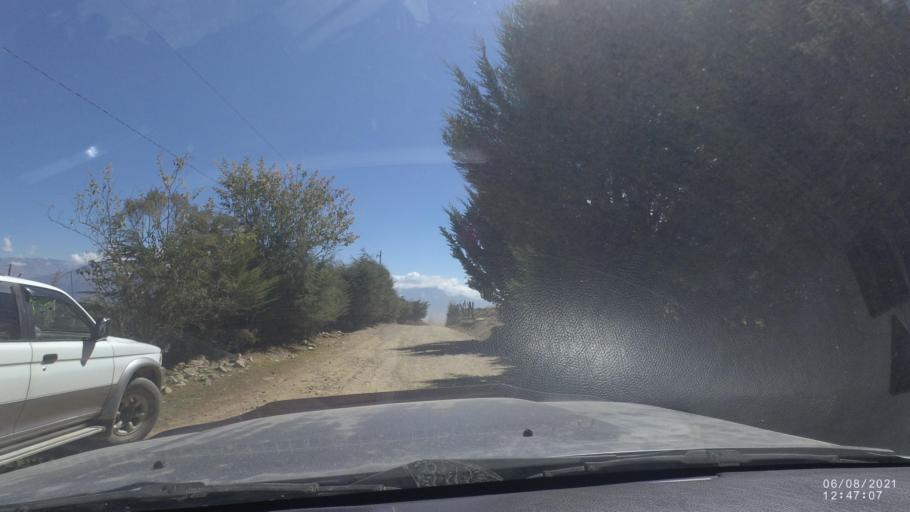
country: BO
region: Cochabamba
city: Colchani
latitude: -16.7619
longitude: -66.6680
